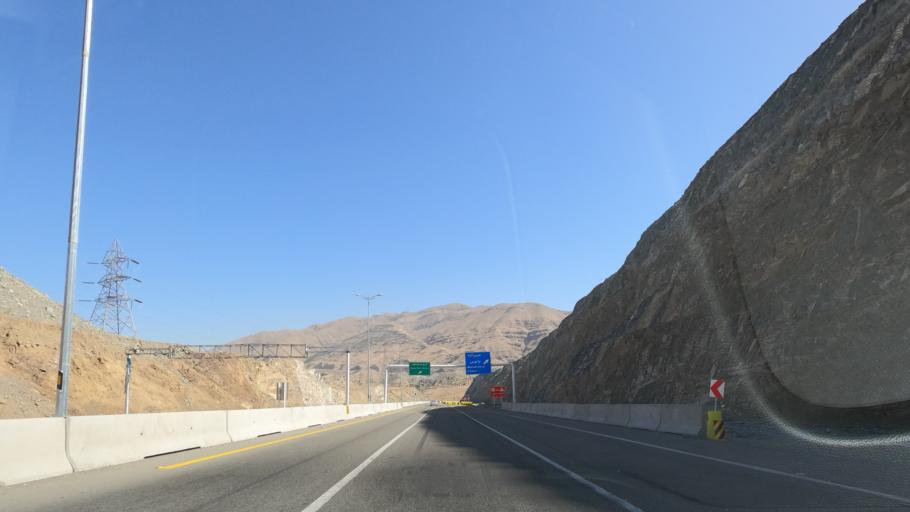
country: IR
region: Alborz
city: Karaj
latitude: 35.8184
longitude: 51.0378
